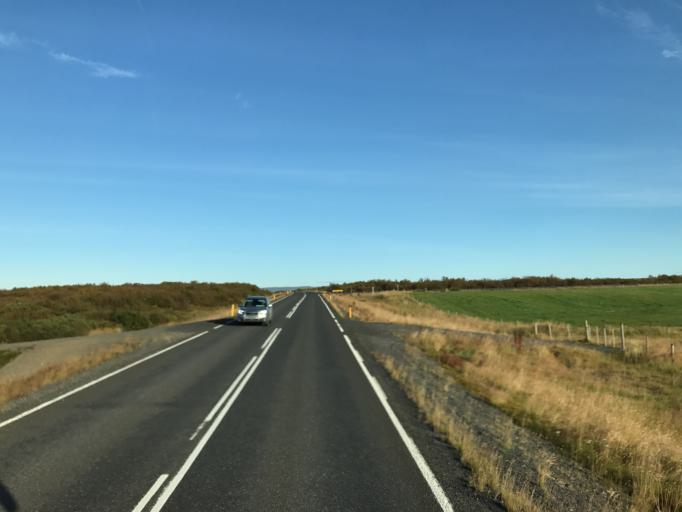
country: IS
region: South
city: Selfoss
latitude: 64.2250
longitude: -20.5900
